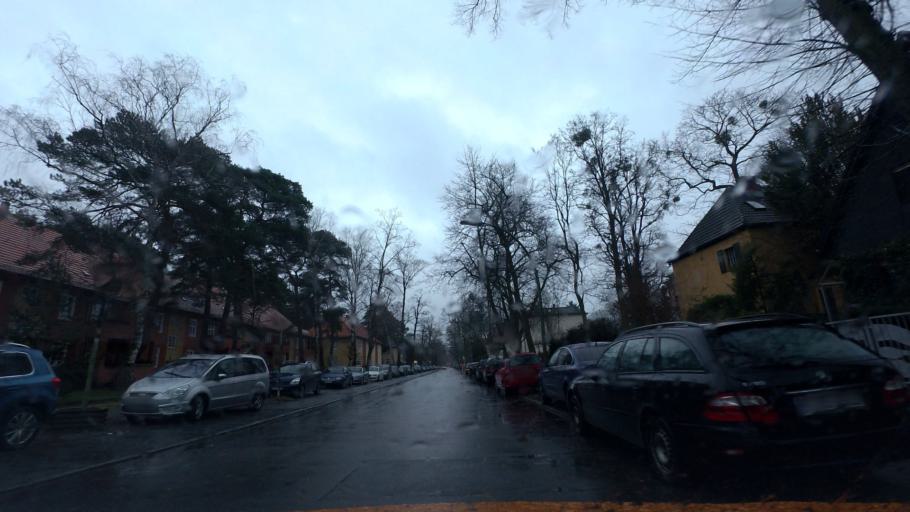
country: DE
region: Berlin
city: Zehlendorf Bezirk
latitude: 52.4394
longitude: 13.2472
